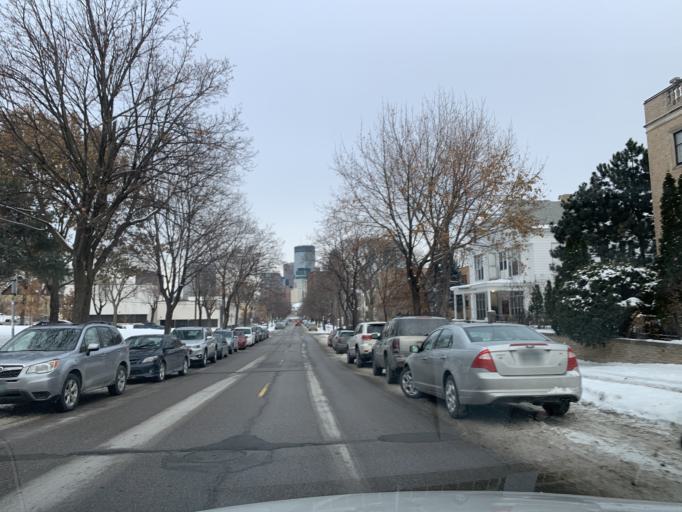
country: US
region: Minnesota
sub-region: Hennepin County
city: Minneapolis
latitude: 44.9600
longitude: -93.2727
